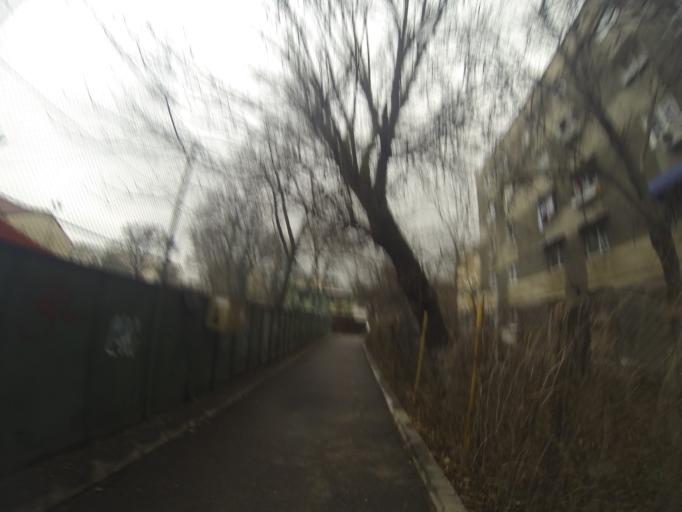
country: RO
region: Bucuresti
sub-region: Municipiul Bucuresti
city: Bucuresti
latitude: 44.4059
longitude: 26.0713
